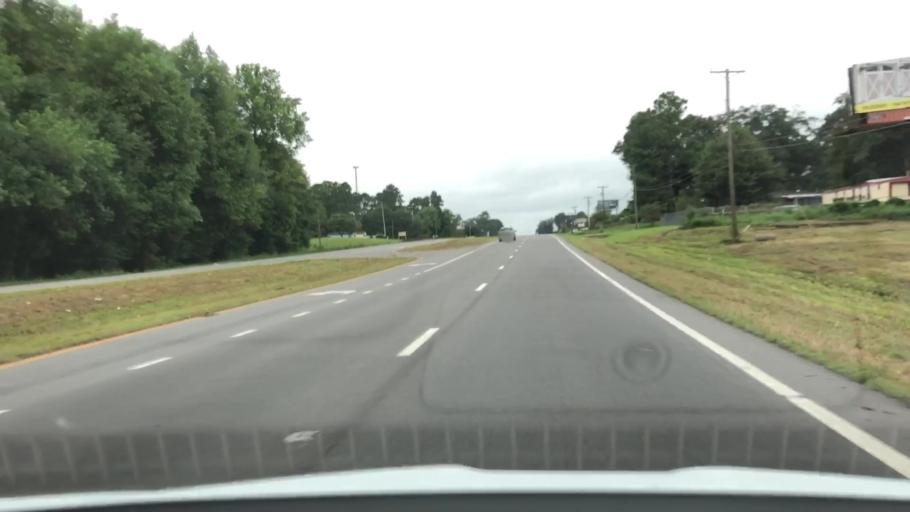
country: US
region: North Carolina
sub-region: Lenoir County
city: La Grange
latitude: 35.2753
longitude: -77.7454
